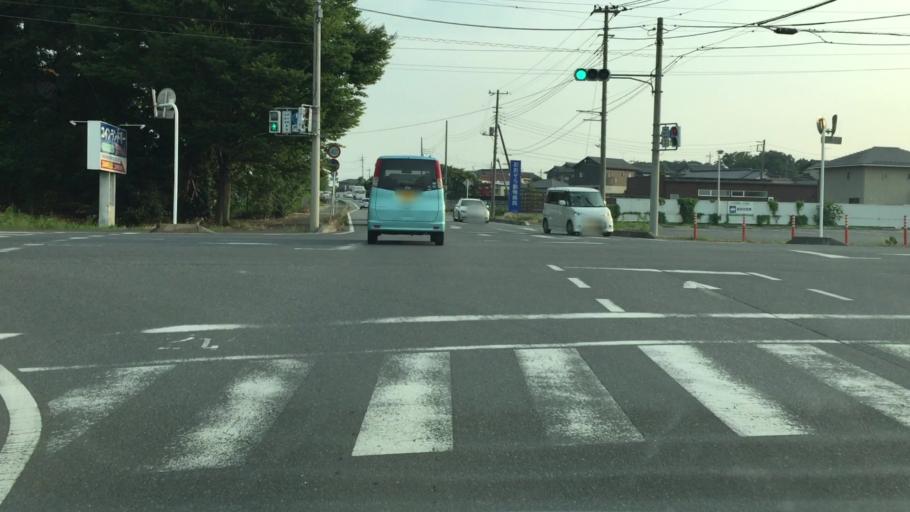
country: JP
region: Gunma
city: Tatebayashi
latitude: 36.2370
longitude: 139.5912
